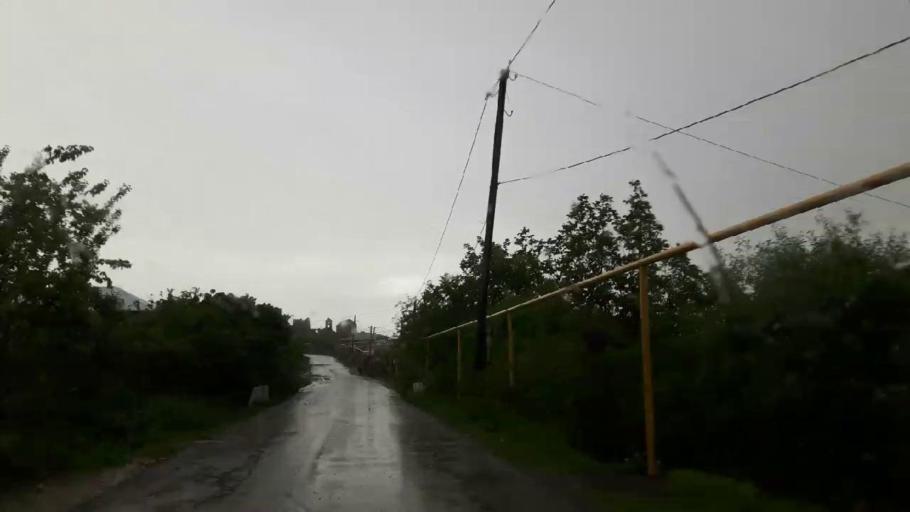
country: GE
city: Agara
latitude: 42.0173
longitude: 43.8373
